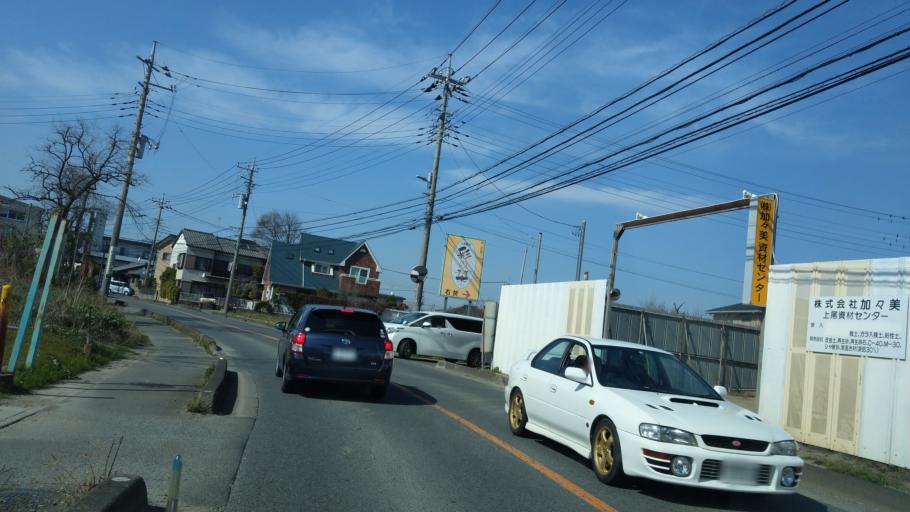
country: JP
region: Saitama
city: Okegawa
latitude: 35.9375
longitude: 139.5563
